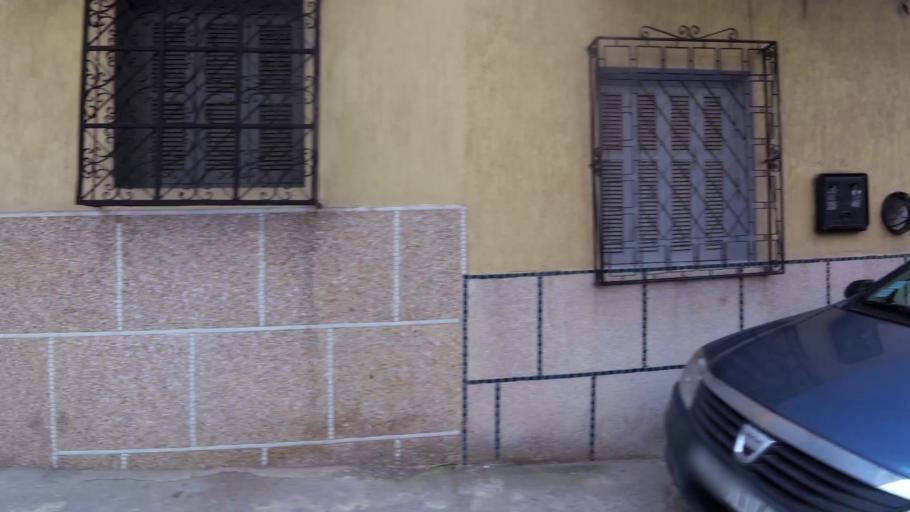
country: MA
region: Tanger-Tetouan
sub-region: Tanger-Assilah
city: Tangier
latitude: 35.7691
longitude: -5.8219
